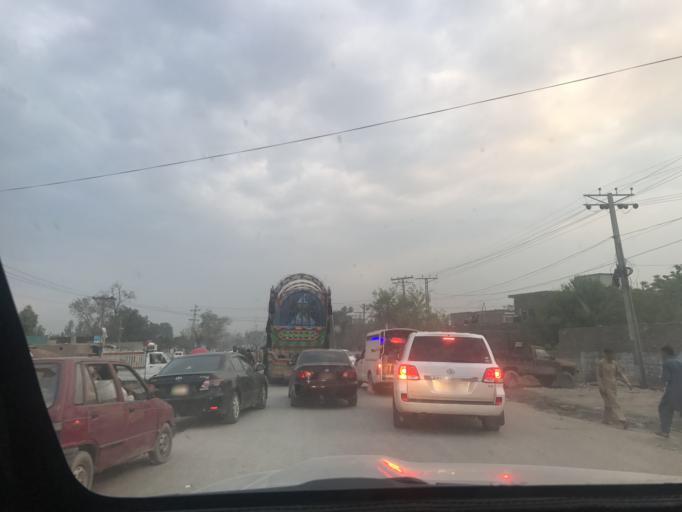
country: PK
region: Khyber Pakhtunkhwa
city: Peshawar
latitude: 33.9969
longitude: 71.4231
